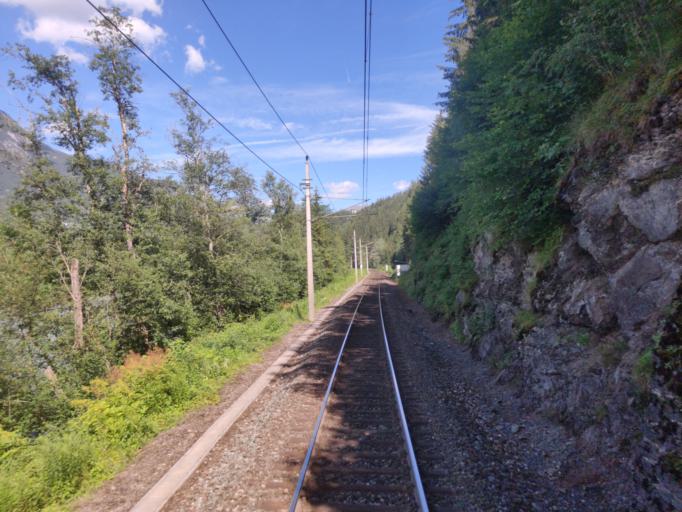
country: AT
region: Tyrol
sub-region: Politischer Bezirk Imst
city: Karrosten
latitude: 47.2158
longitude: 10.7388
